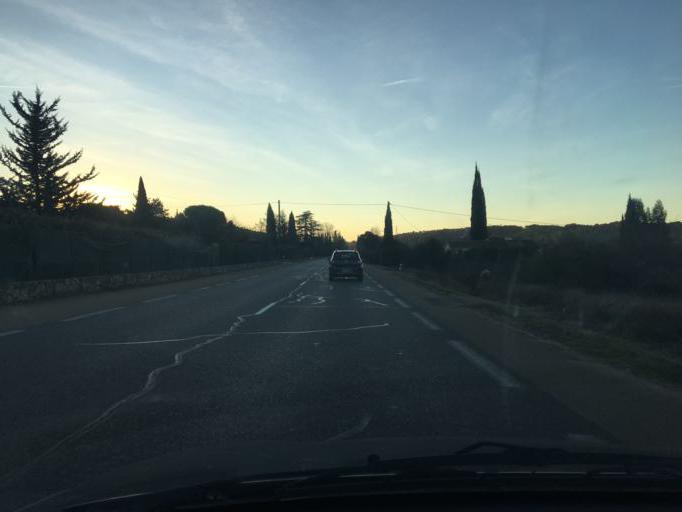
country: FR
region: Provence-Alpes-Cote d'Azur
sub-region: Departement du Var
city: Lorgues
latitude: 43.4838
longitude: 6.3686
